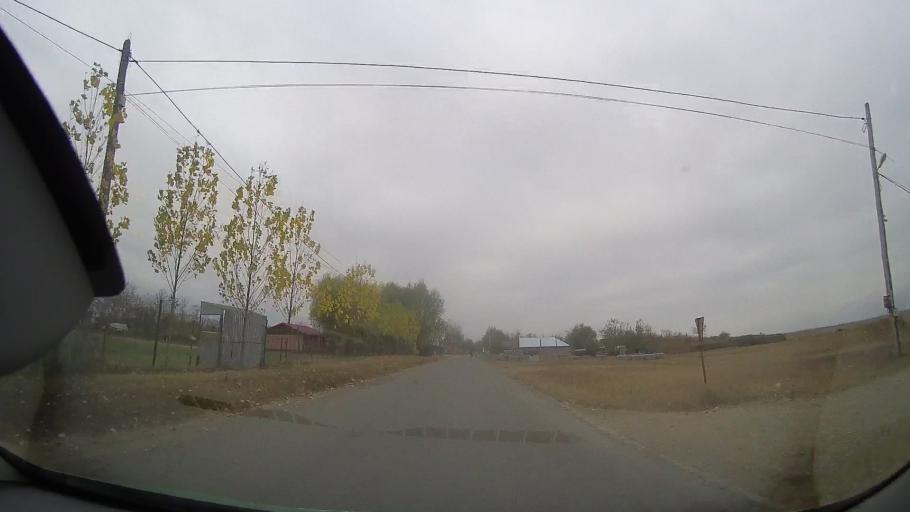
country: RO
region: Buzau
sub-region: Comuna Luciu
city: Luciu
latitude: 44.9681
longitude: 27.0936
